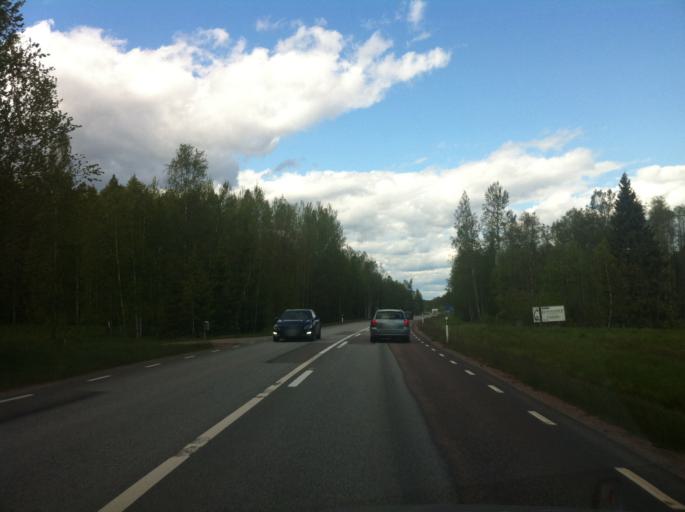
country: SE
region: Vaermland
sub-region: Storfors Kommun
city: Storfors
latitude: 59.4247
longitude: 14.2228
